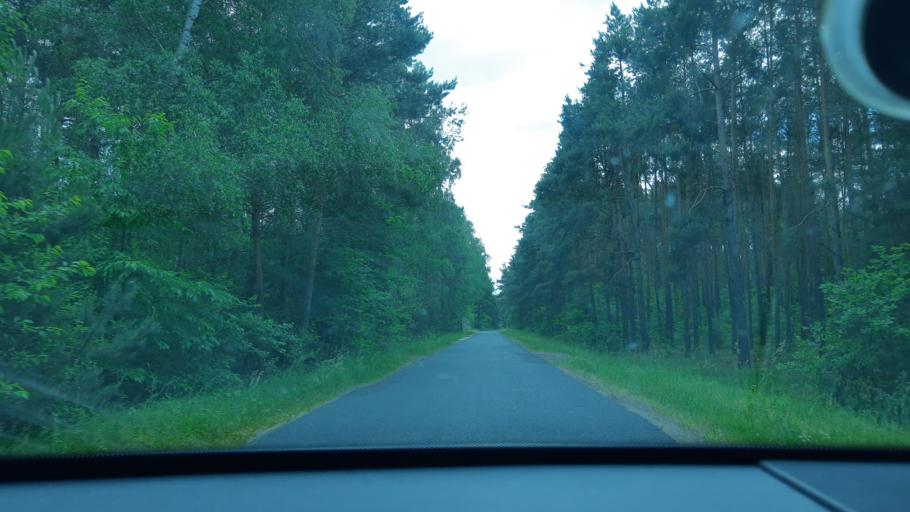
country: PL
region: Lodz Voivodeship
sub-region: Powiat sieradzki
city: Burzenin
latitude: 51.4989
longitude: 18.8463
